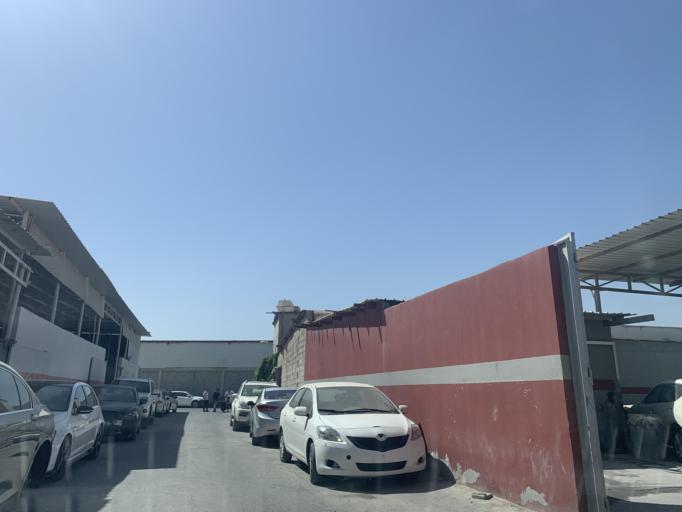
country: BH
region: Manama
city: Jidd Hafs
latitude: 26.2241
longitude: 50.5304
